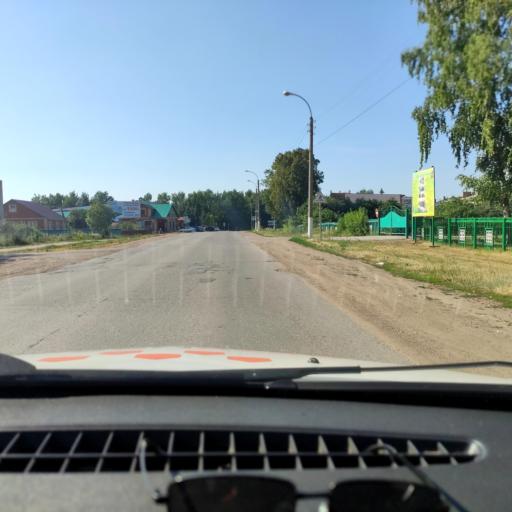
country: RU
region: Bashkortostan
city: Tolbazy
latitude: 54.0095
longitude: 55.8884
